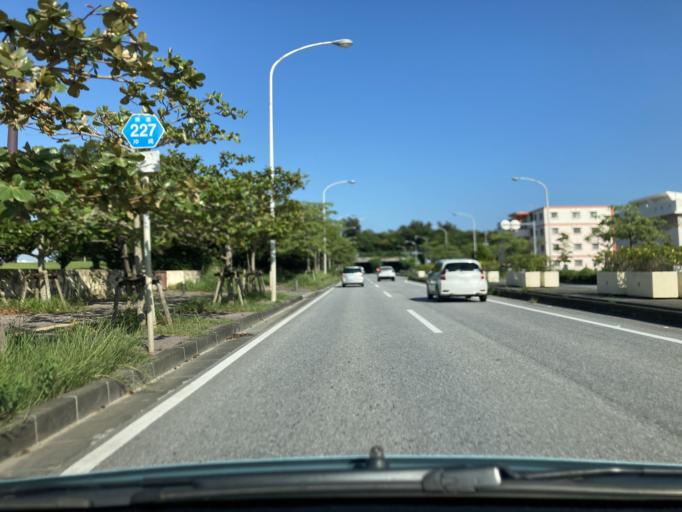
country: JP
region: Okinawa
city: Okinawa
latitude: 26.3069
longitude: 127.8208
